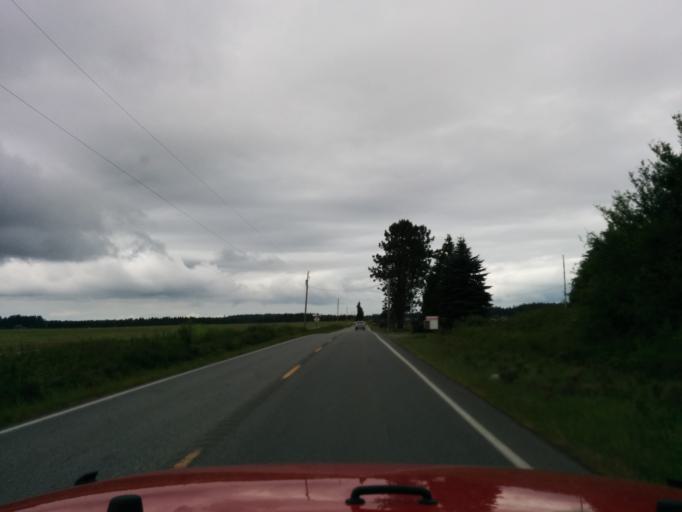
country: US
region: Washington
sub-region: Island County
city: Coupeville
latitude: 48.1906
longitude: -122.6267
